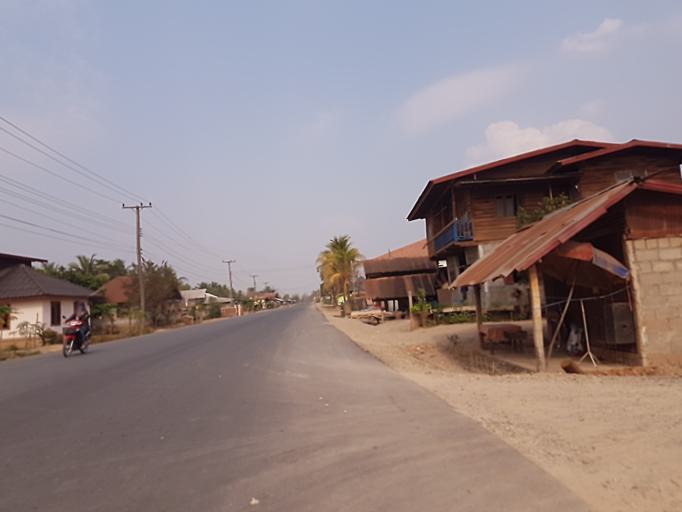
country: TH
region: Nong Khai
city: Nong Khai
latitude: 17.9702
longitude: 102.8431
